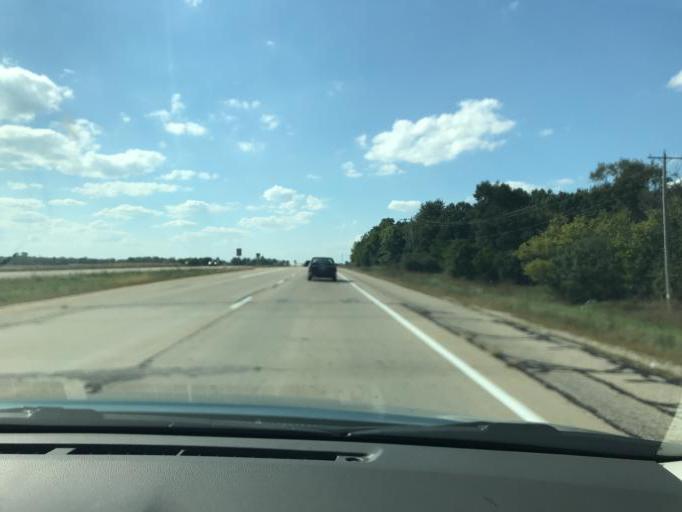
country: US
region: Wisconsin
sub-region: Kenosha County
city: Powers Lake
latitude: 42.5823
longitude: -88.2681
